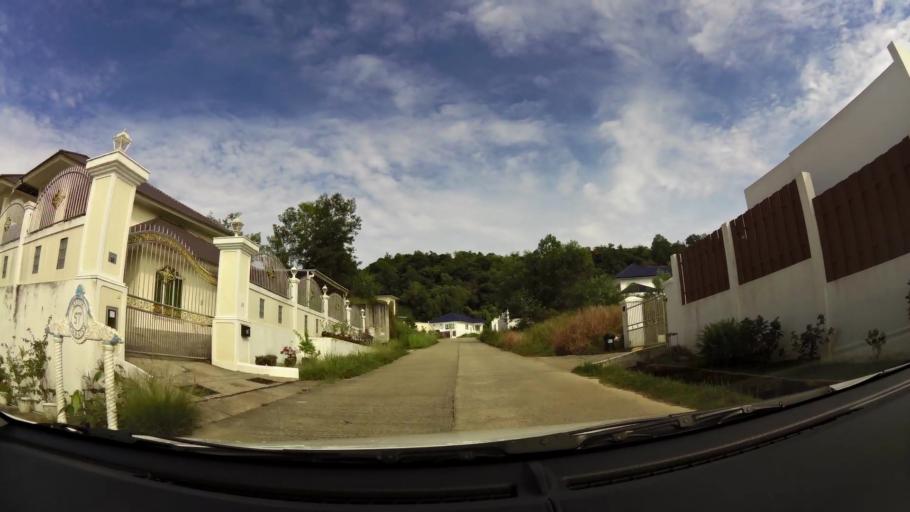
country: BN
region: Brunei and Muara
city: Bandar Seri Begawan
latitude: 4.8980
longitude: 114.9650
